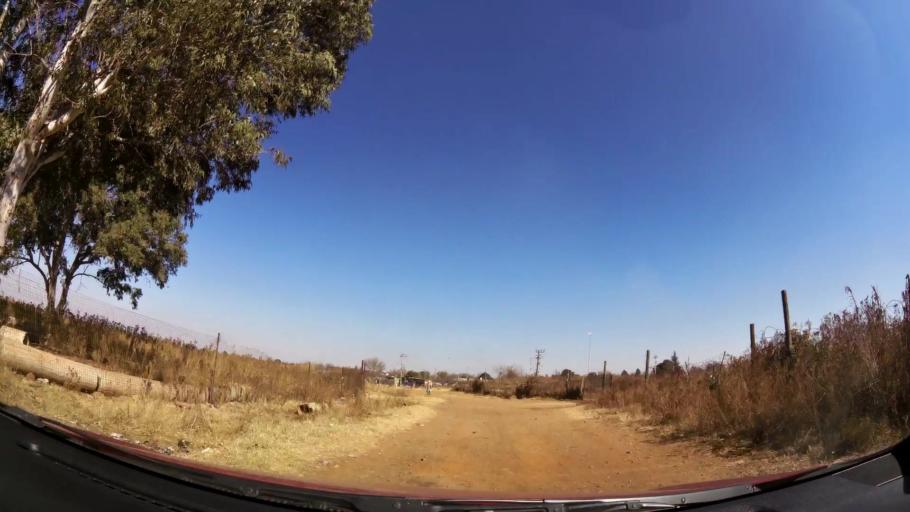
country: ZA
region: Gauteng
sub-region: City of Johannesburg Metropolitan Municipality
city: Soweto
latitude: -26.2165
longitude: 27.8426
